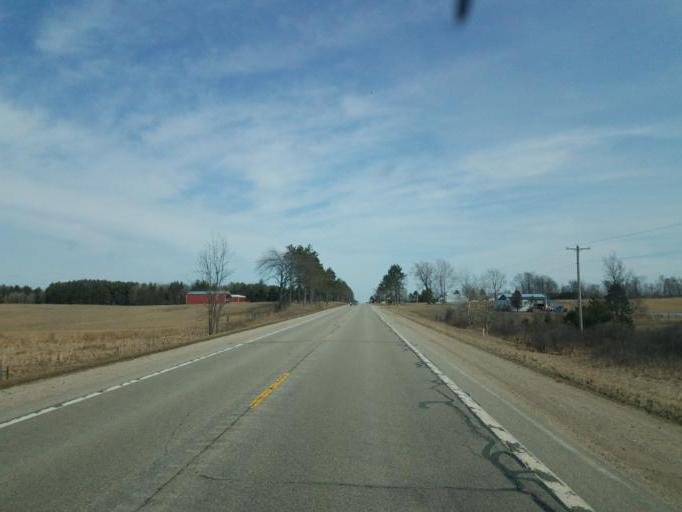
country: US
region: Michigan
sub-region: Osceola County
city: Evart
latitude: 43.9007
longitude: -85.1591
